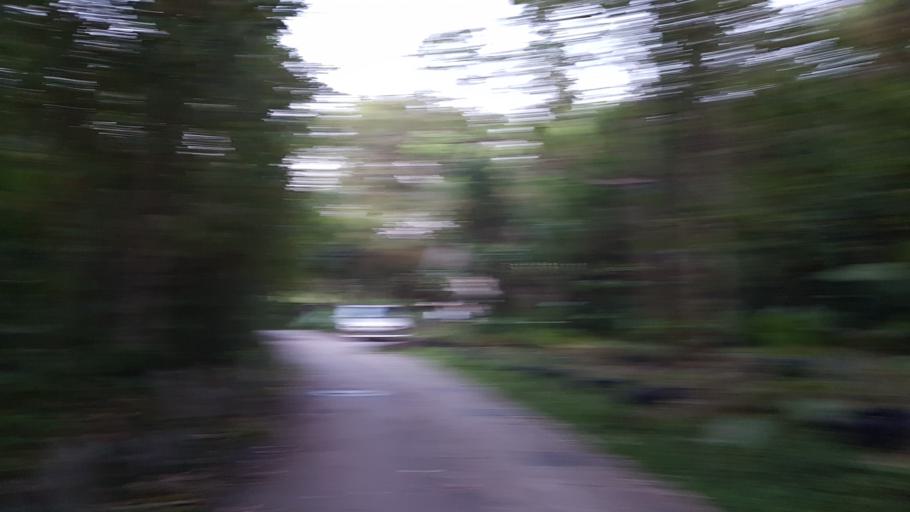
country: TW
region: Taiwan
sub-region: Yilan
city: Yilan
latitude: 24.9340
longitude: 121.7044
